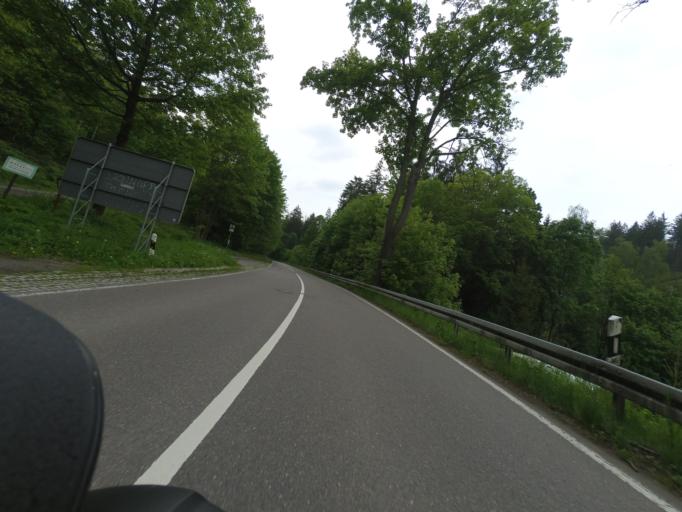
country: DE
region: Saxony
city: Wolkenstein
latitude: 50.6700
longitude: 13.0649
